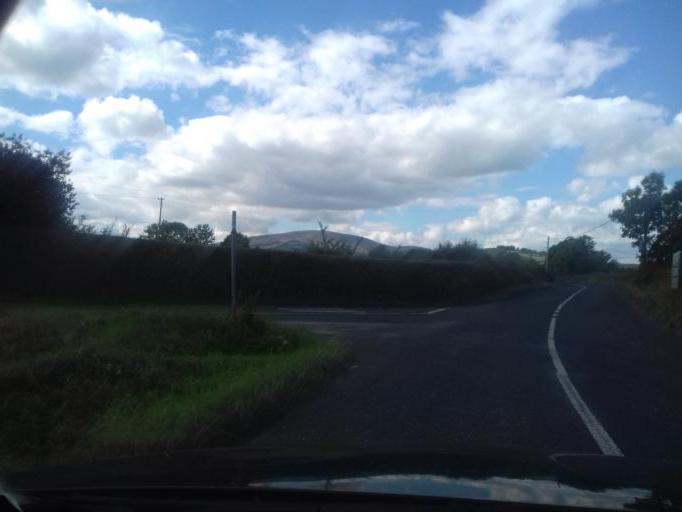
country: IE
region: Munster
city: Carrick-on-Suir
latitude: 52.3853
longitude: -7.4648
